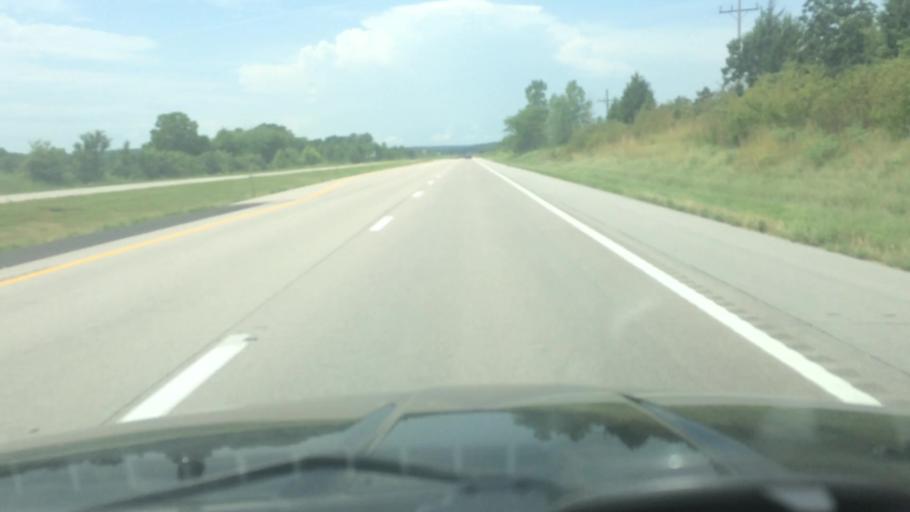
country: US
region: Missouri
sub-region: Polk County
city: Humansville
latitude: 37.8034
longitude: -93.5975
